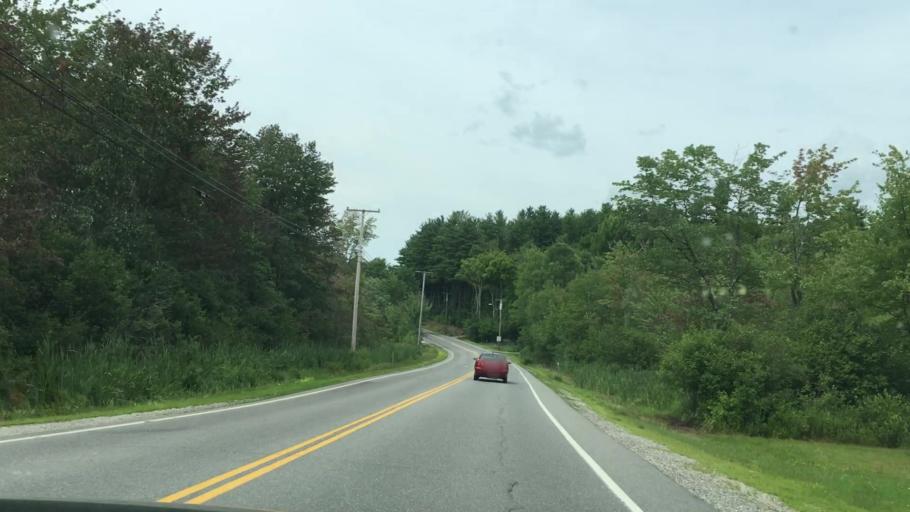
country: US
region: New Hampshire
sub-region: Cheshire County
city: Jaffrey
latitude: 42.8073
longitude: -72.0284
